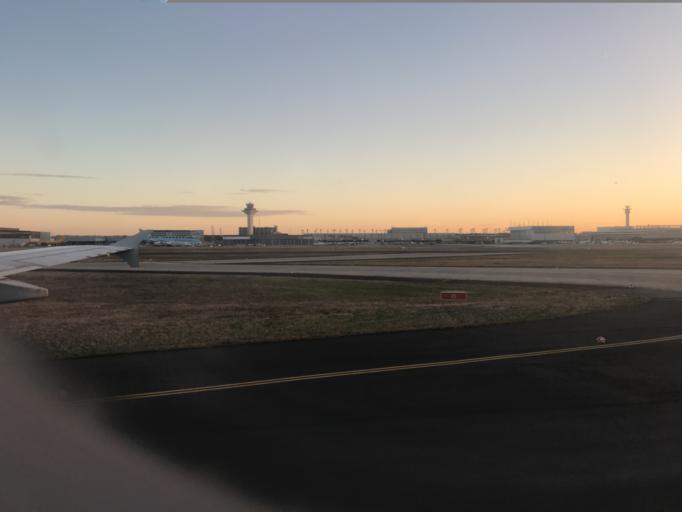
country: DE
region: Hesse
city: Kelsterbach
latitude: 50.0357
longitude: 8.5575
